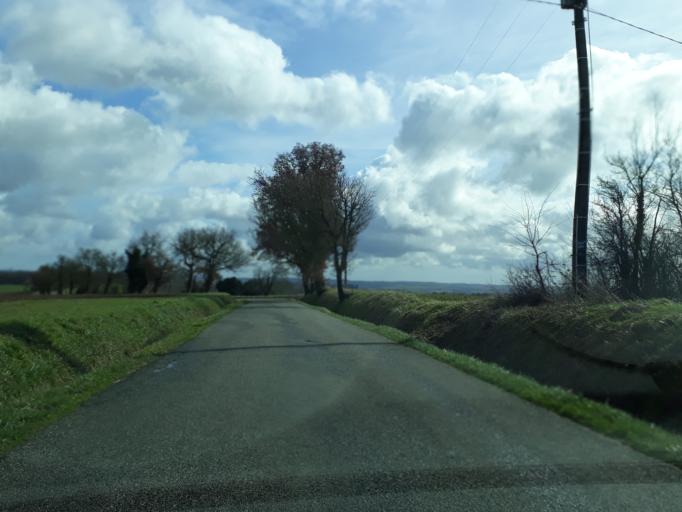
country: FR
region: Midi-Pyrenees
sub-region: Departement du Gers
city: Gimont
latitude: 43.6336
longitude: 1.0075
